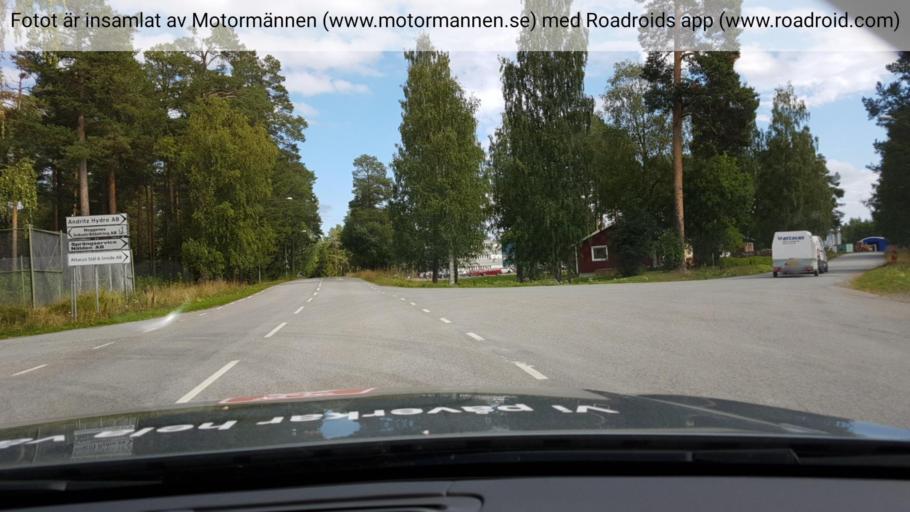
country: SE
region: Jaemtland
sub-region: Krokoms Kommun
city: Krokom
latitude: 63.3345
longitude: 14.2138
